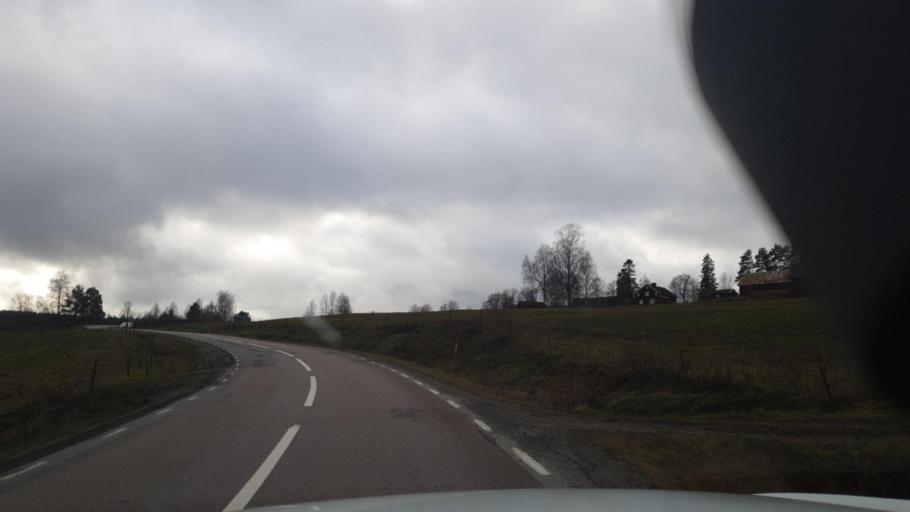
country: SE
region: Vaermland
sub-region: Sunne Kommun
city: Sunne
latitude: 59.6673
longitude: 13.0088
